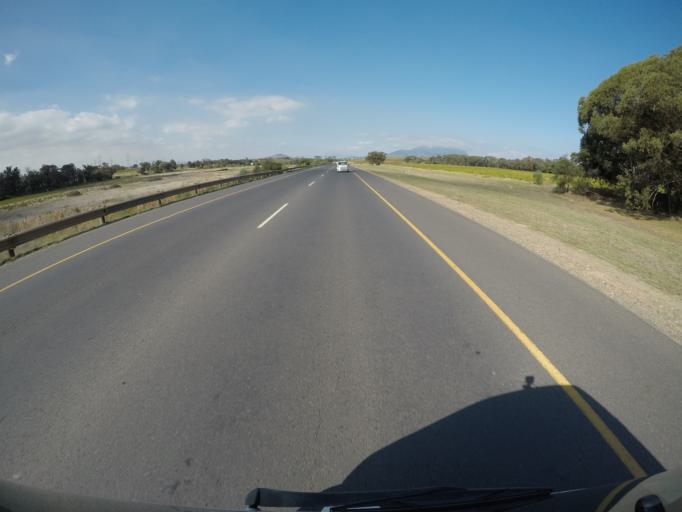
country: ZA
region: Western Cape
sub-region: City of Cape Town
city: Kraaifontein
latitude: -33.8831
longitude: 18.7546
